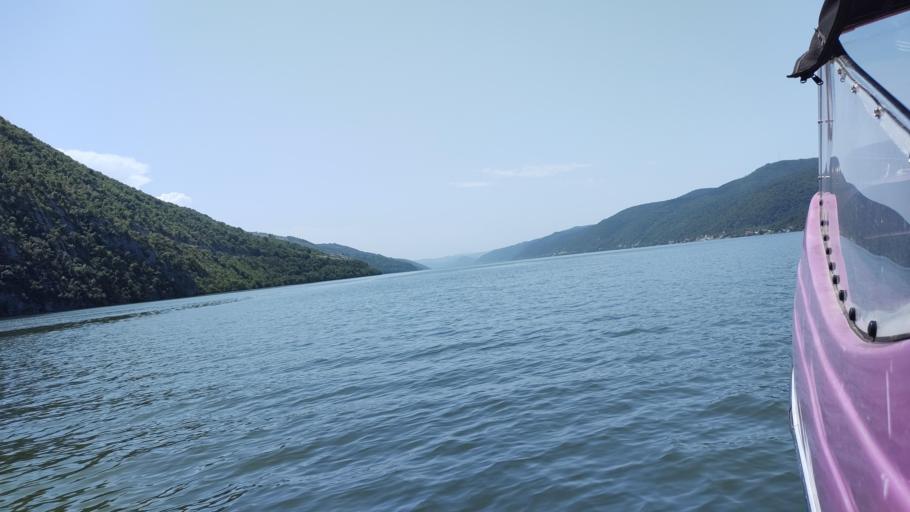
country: RO
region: Mehedinti
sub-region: Comuna Dubova
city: Dubova
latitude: 44.5851
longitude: 22.2525
